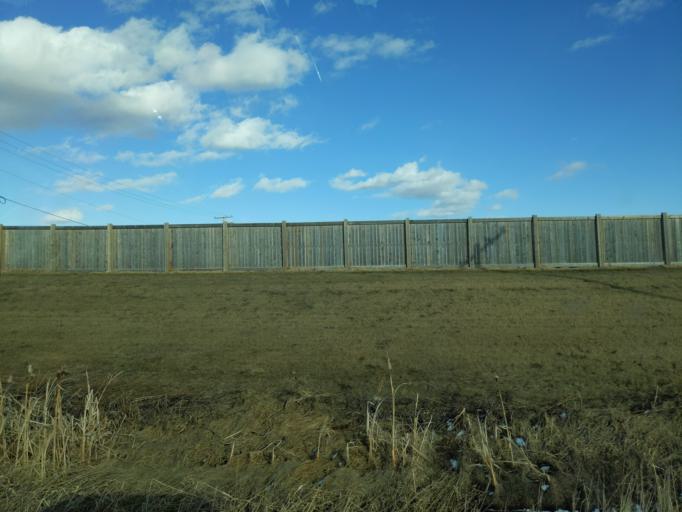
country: CA
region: Saskatchewan
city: Lloydminster
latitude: 53.2452
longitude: -109.9791
